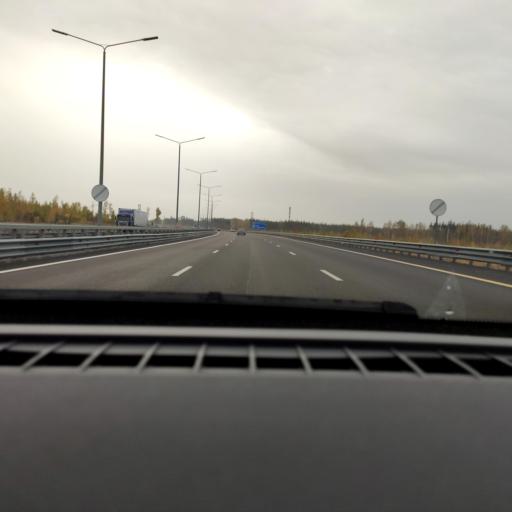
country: RU
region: Voronezj
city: Somovo
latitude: 51.7516
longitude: 39.3050
